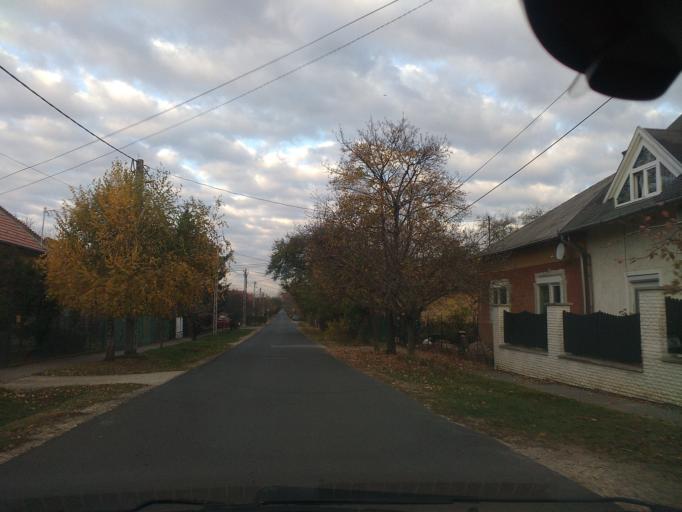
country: HU
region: Budapest
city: Budapest XVIII. keruelet
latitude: 47.4341
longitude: 19.2104
